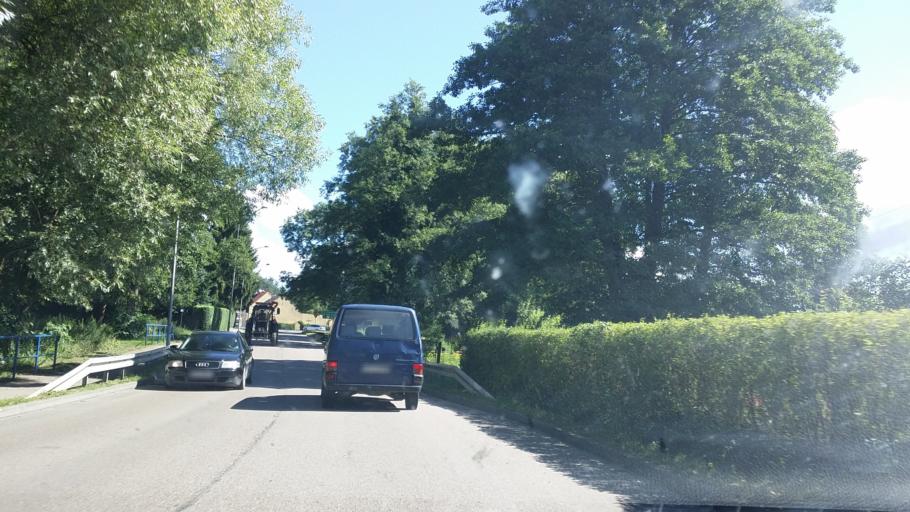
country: PL
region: West Pomeranian Voivodeship
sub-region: Powiat drawski
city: Kalisz Pomorski
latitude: 53.3003
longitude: 15.9080
